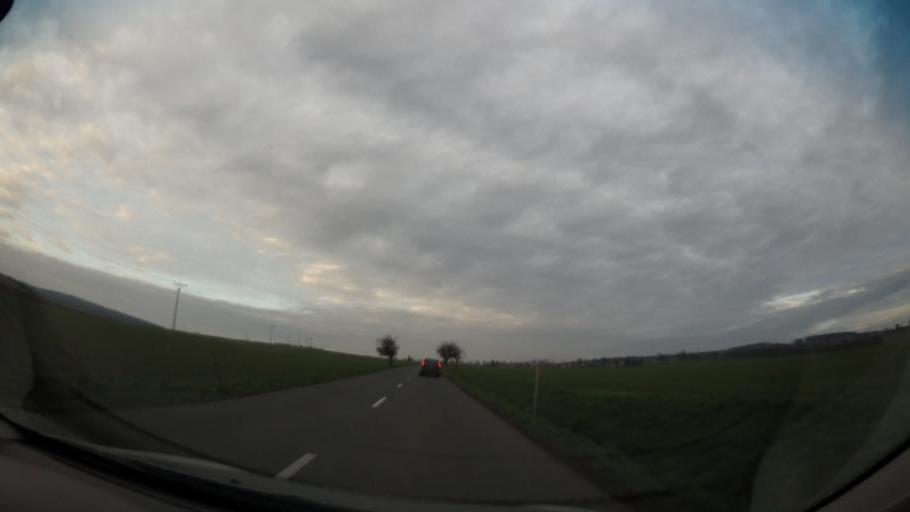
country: CZ
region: South Moravian
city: Oslavany
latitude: 49.1277
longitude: 16.3470
